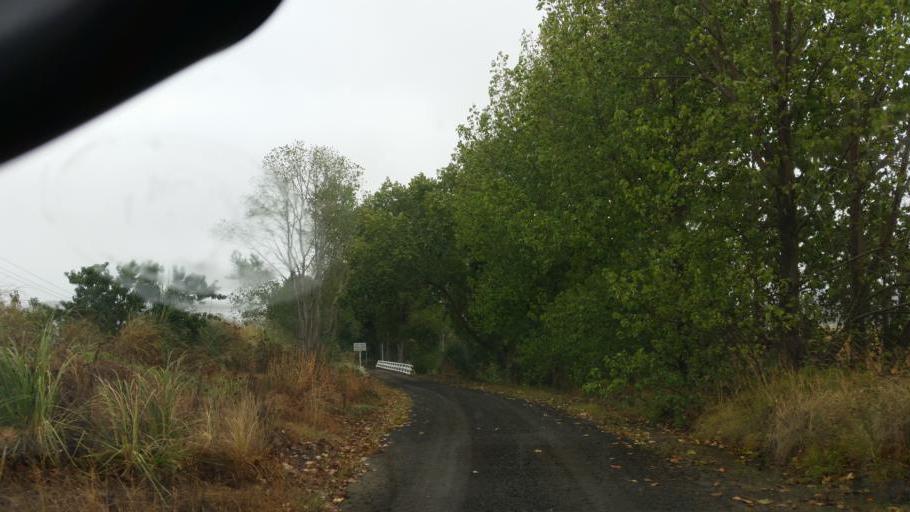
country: NZ
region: Northland
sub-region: Kaipara District
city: Dargaville
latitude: -35.8313
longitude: 173.7494
